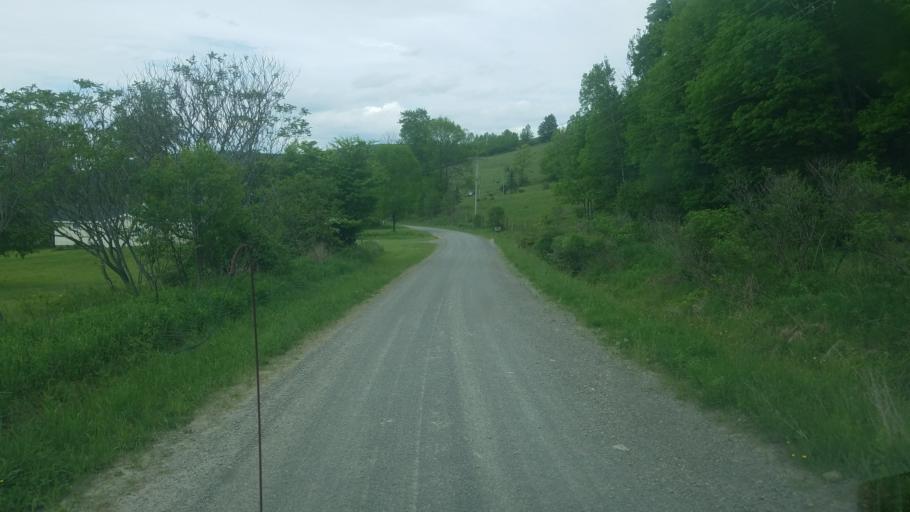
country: US
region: Pennsylvania
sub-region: Tioga County
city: Westfield
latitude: 41.8708
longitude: -77.5966
